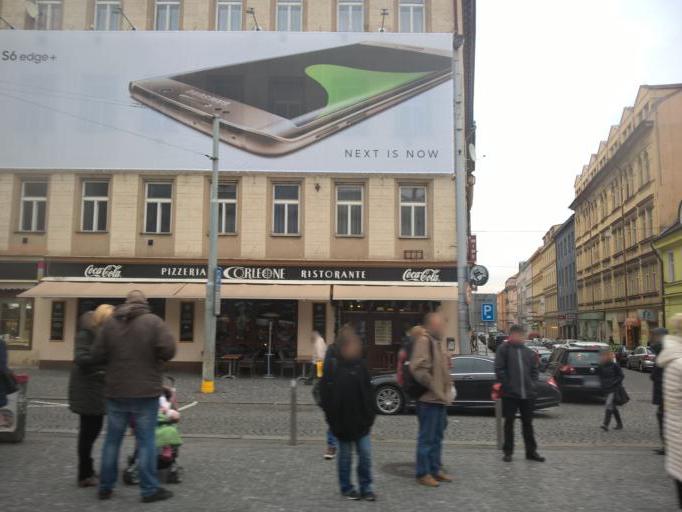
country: CZ
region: Praha
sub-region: Praha 2
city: Vysehrad
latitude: 50.0716
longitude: 14.4042
